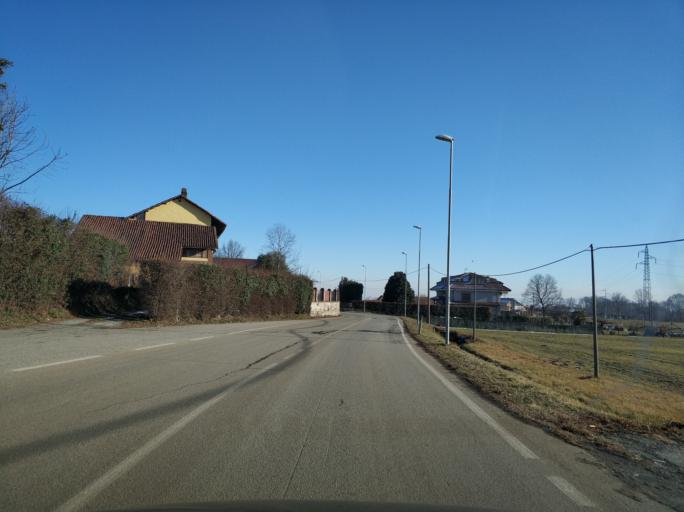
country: IT
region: Piedmont
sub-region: Provincia di Torino
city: San Francesco al Campo
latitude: 45.2245
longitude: 7.6559
